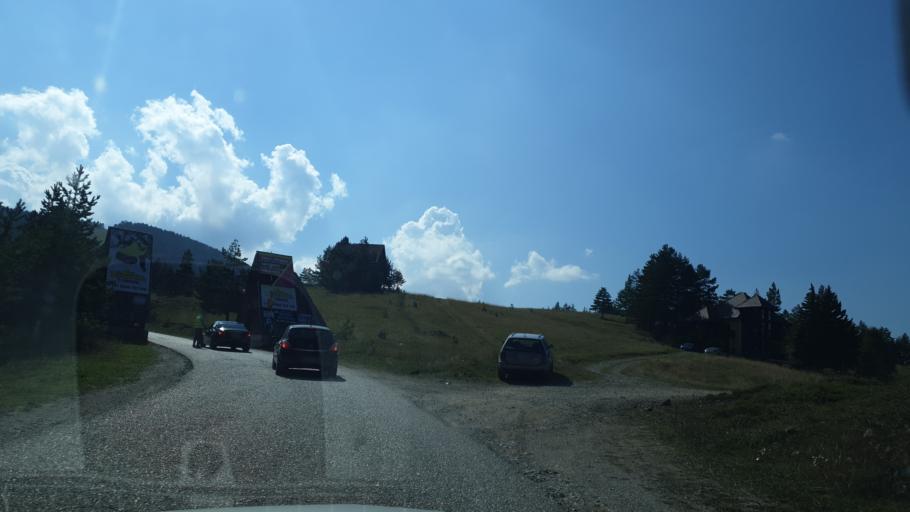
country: RS
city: Zlatibor
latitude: 43.6730
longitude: 19.6500
